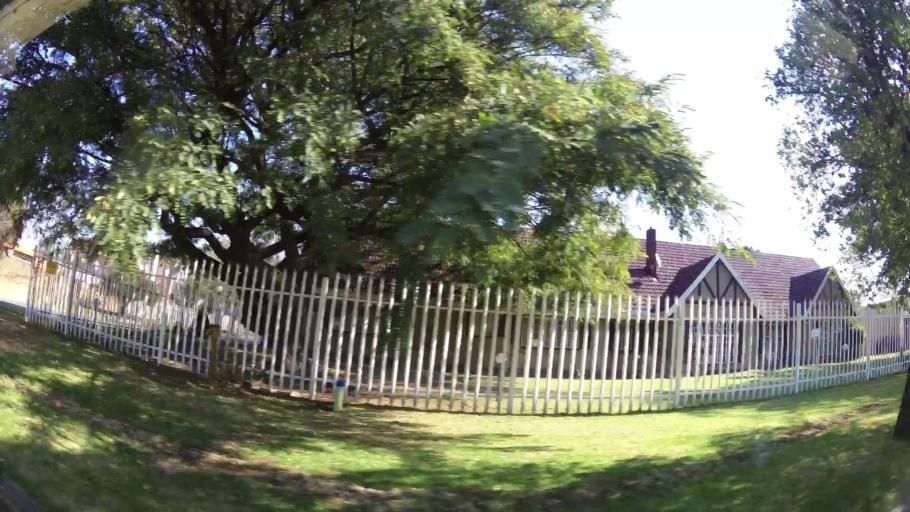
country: ZA
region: Gauteng
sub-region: Ekurhuleni Metropolitan Municipality
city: Boksburg
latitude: -26.2497
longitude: 28.2705
